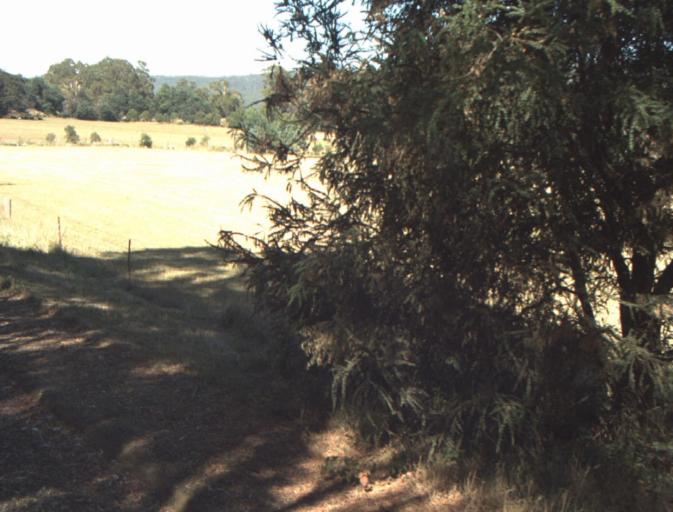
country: AU
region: Tasmania
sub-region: Launceston
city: Newstead
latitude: -41.3147
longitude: 147.3206
